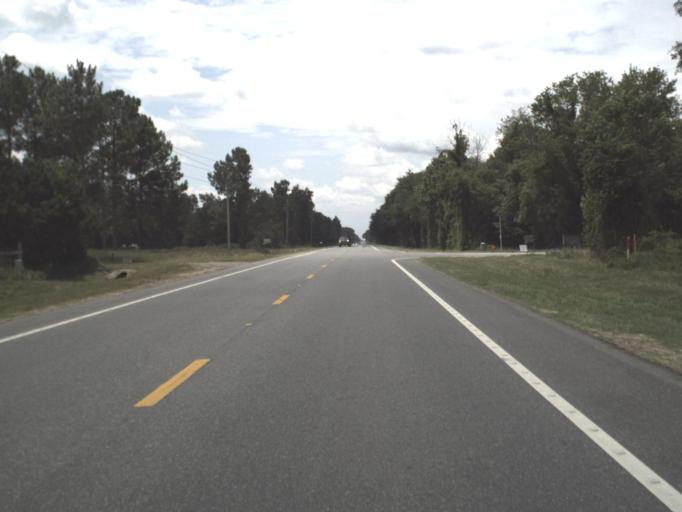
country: US
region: Florida
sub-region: Suwannee County
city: Wellborn
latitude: 30.1162
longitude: -82.9492
